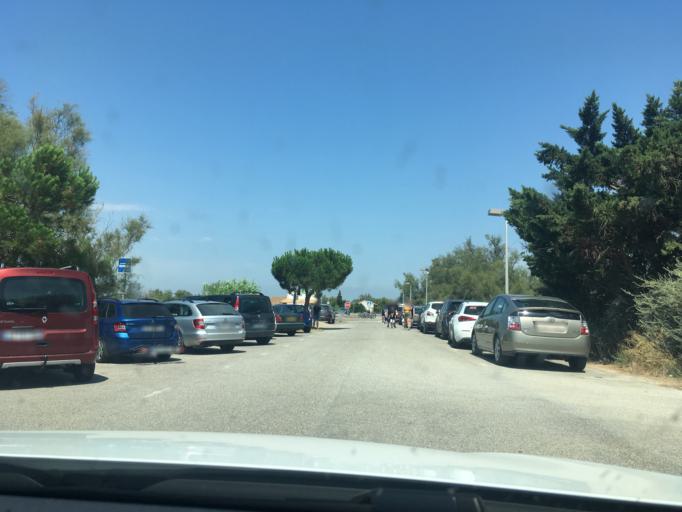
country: FR
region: Provence-Alpes-Cote d'Azur
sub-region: Departement des Bouches-du-Rhone
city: Saintes-Maries-de-la-Mer
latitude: 43.4881
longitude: 4.4043
